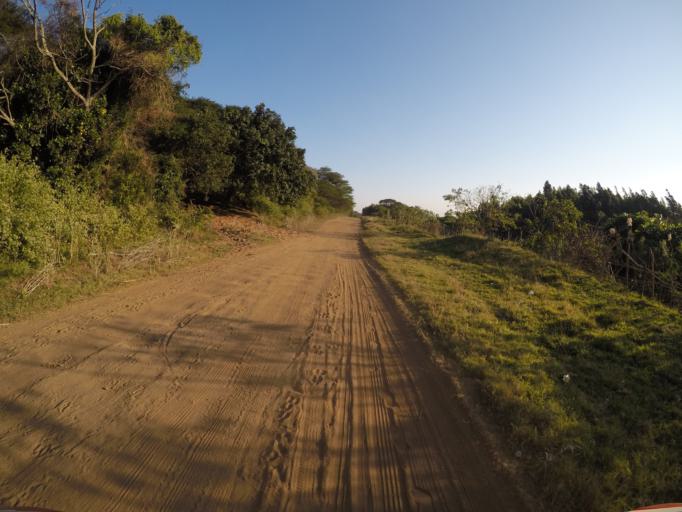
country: ZA
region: KwaZulu-Natal
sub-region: uThungulu District Municipality
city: KwaMbonambi
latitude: -28.7003
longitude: 32.1923
